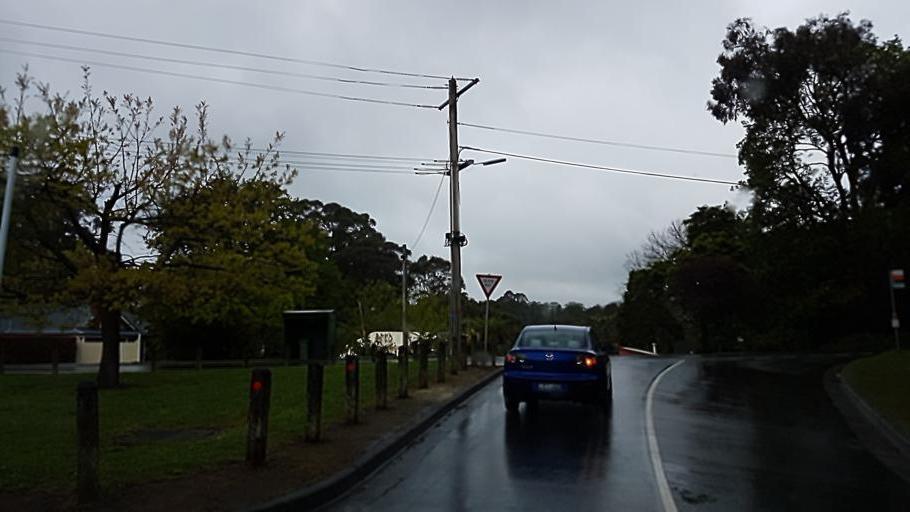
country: AU
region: Victoria
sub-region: Yarra Ranges
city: Monbulk
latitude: -37.8823
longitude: 145.3955
